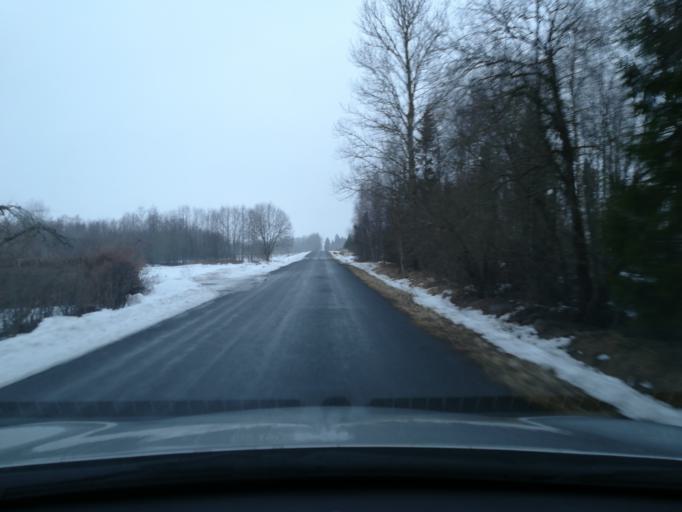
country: EE
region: Harju
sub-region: Raasiku vald
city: Raasiku
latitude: 59.3436
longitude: 25.2230
